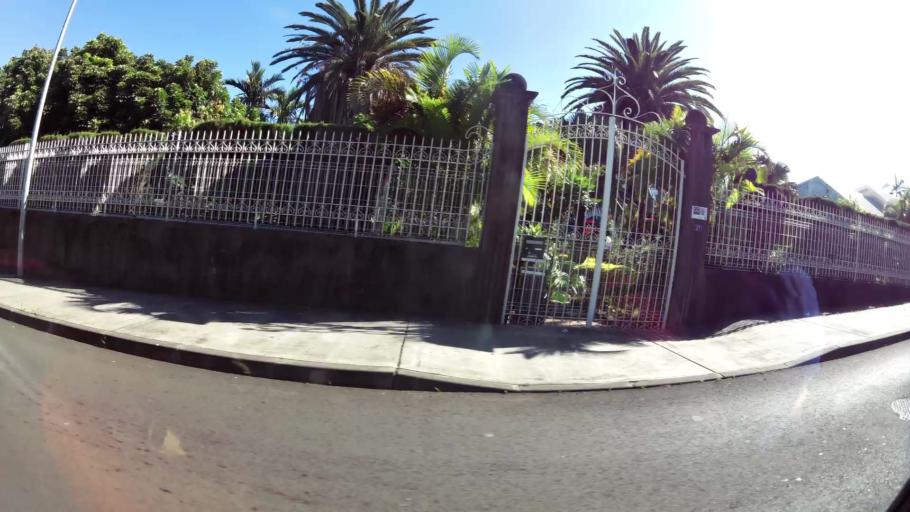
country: RE
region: Reunion
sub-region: Reunion
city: Le Tampon
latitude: -21.2728
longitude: 55.5149
